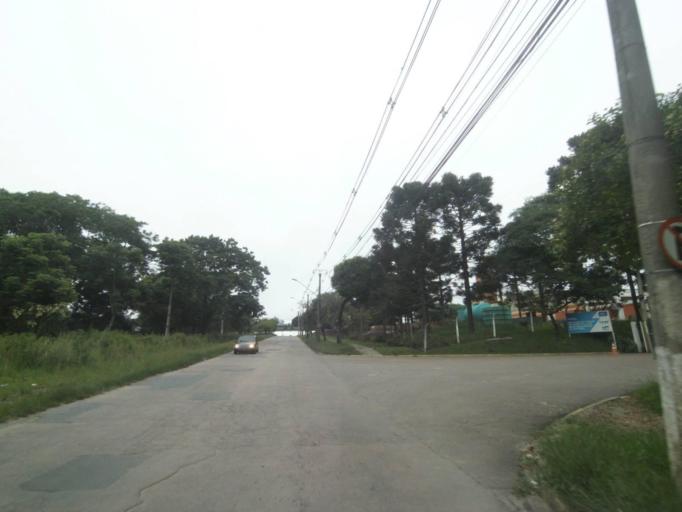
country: BR
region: Parana
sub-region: Araucaria
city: Araucaria
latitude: -25.5365
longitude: -49.3182
